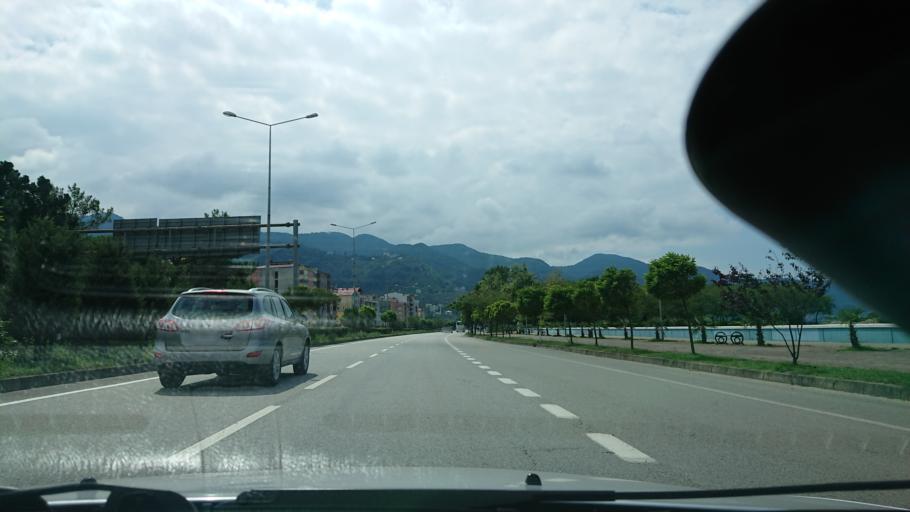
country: TR
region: Trabzon
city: Espiye
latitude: 40.9483
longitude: 38.6996
